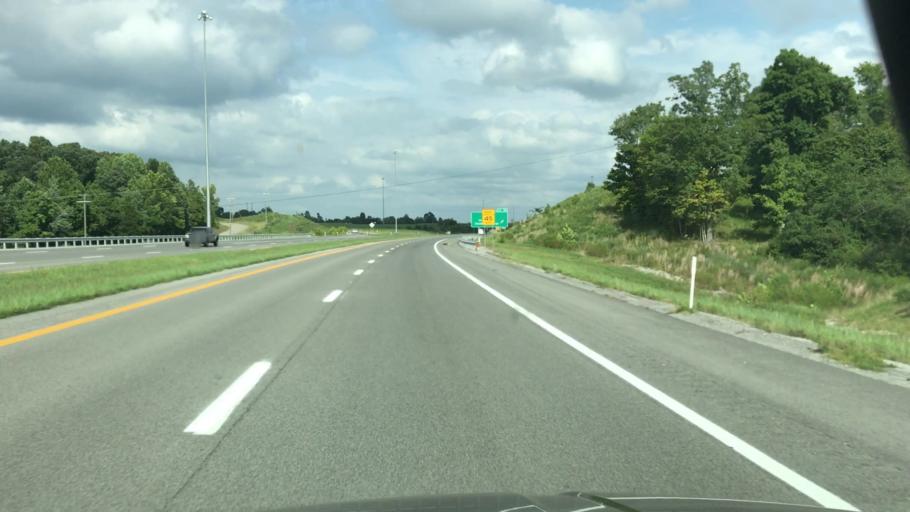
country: US
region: Kentucky
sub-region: Hopkins County
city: Dawson Springs
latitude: 37.1970
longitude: -87.6963
